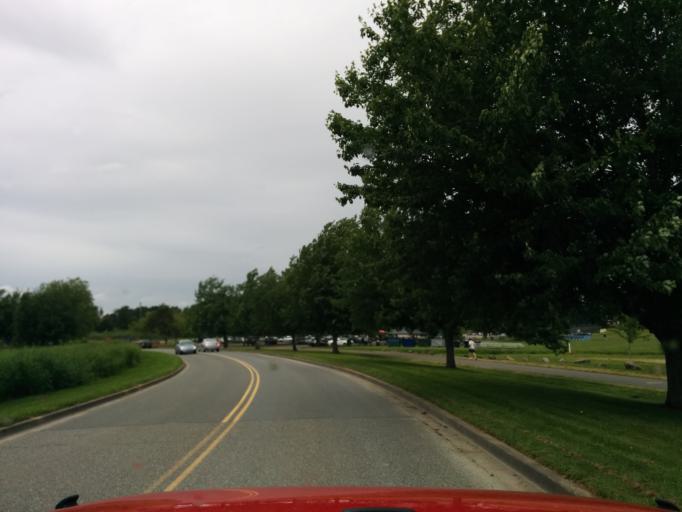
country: US
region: Washington
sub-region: King County
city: Redmond
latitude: 47.6633
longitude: -122.1121
